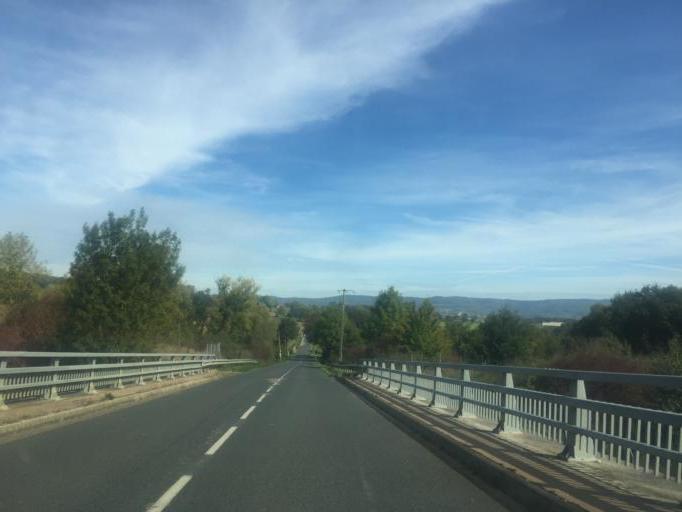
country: FR
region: Franche-Comte
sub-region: Departement du Jura
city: Saint-Amour
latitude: 46.4132
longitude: 5.2773
